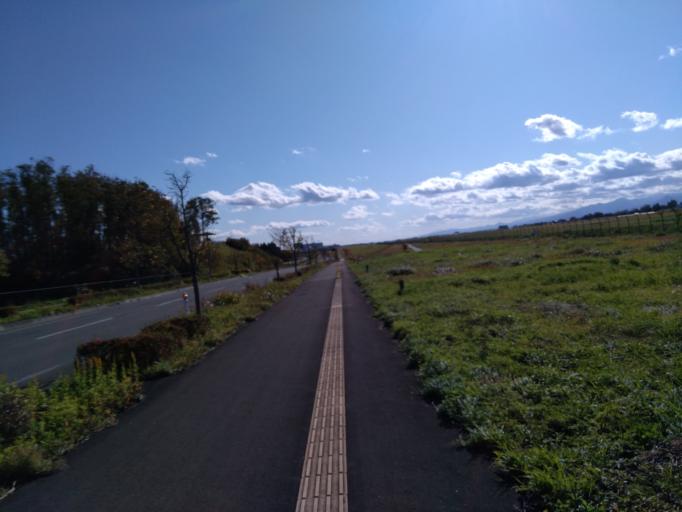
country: JP
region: Iwate
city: Hanamaki
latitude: 39.4343
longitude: 141.1401
